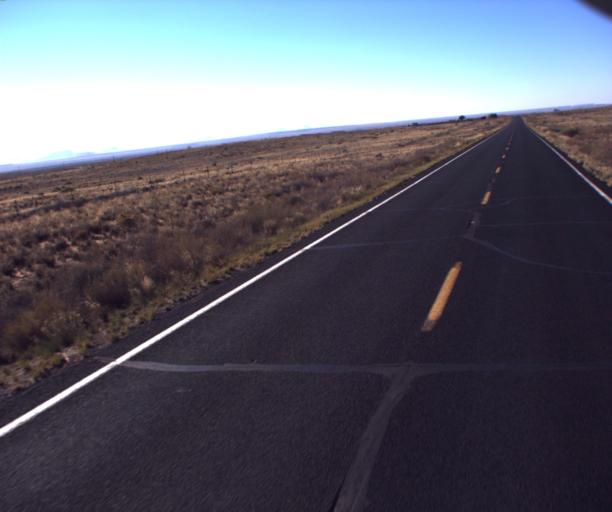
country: US
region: Arizona
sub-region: Navajo County
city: First Mesa
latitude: 35.7803
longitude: -110.5019
